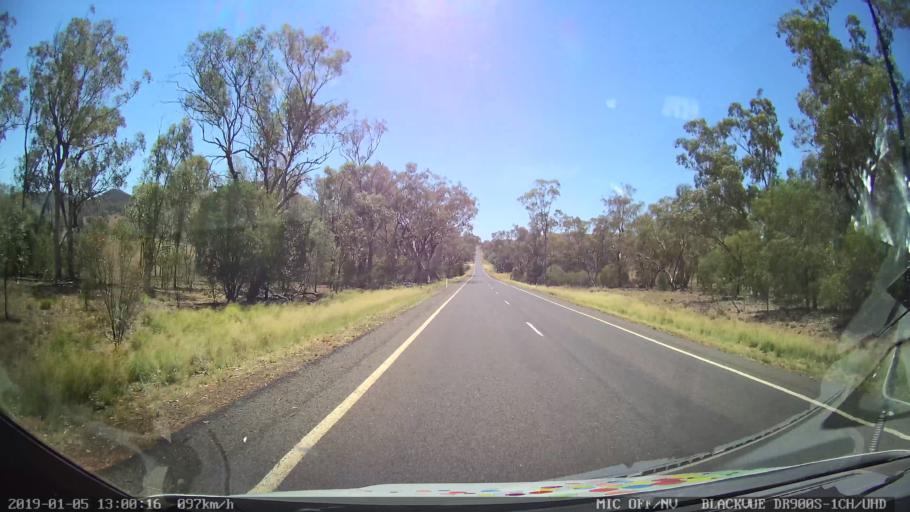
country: AU
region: New South Wales
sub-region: Narrabri
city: Boggabri
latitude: -31.1153
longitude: 149.7792
